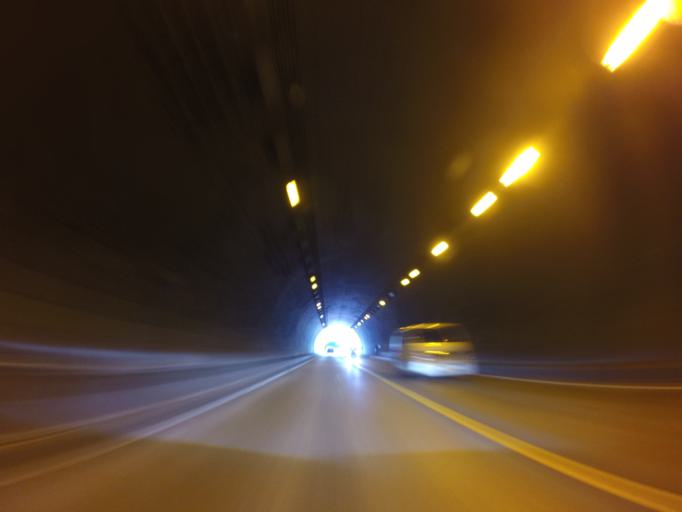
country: JP
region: Shizuoka
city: Mishima
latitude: 35.0336
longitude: 138.9226
